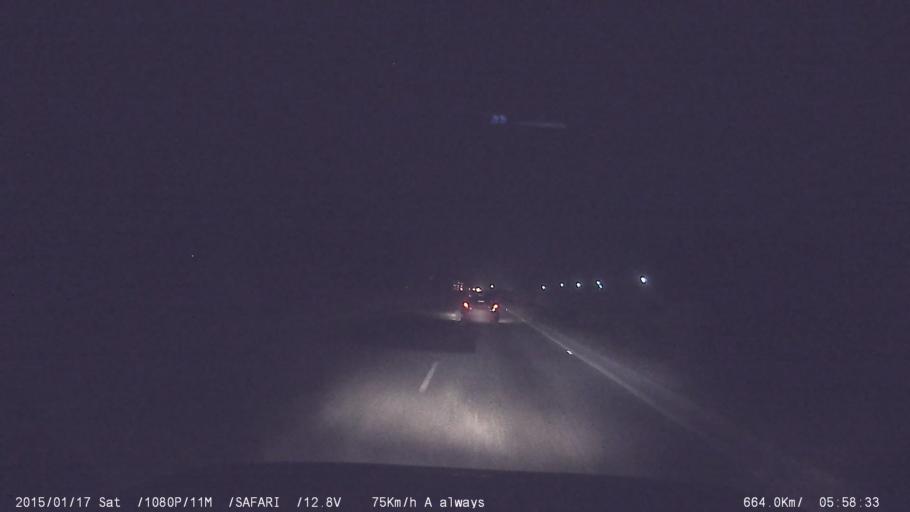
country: IN
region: Tamil Nadu
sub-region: Kancheepuram
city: Kanchipuram
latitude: 12.8985
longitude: 79.5545
